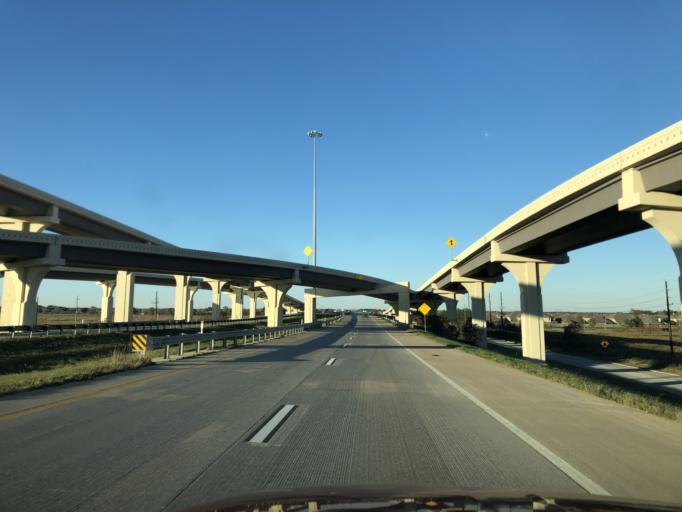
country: US
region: Texas
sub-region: Harris County
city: Cypress
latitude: 29.9998
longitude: -95.7688
